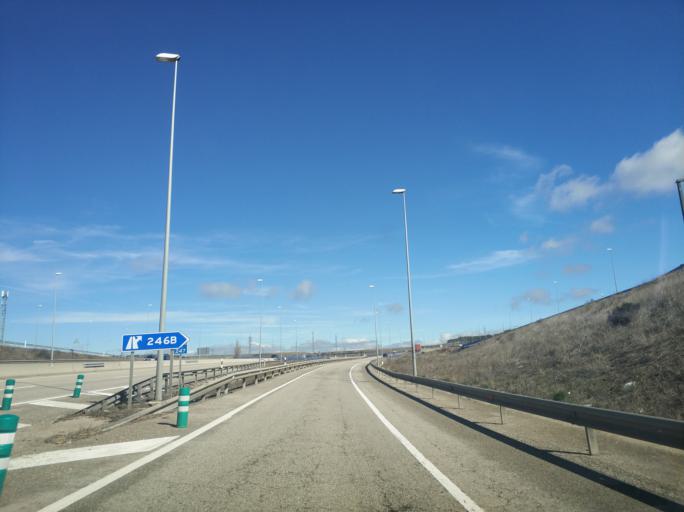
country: ES
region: Castille and Leon
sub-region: Provincia de Burgos
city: Cardenajimeno
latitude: 42.3622
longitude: -3.6399
